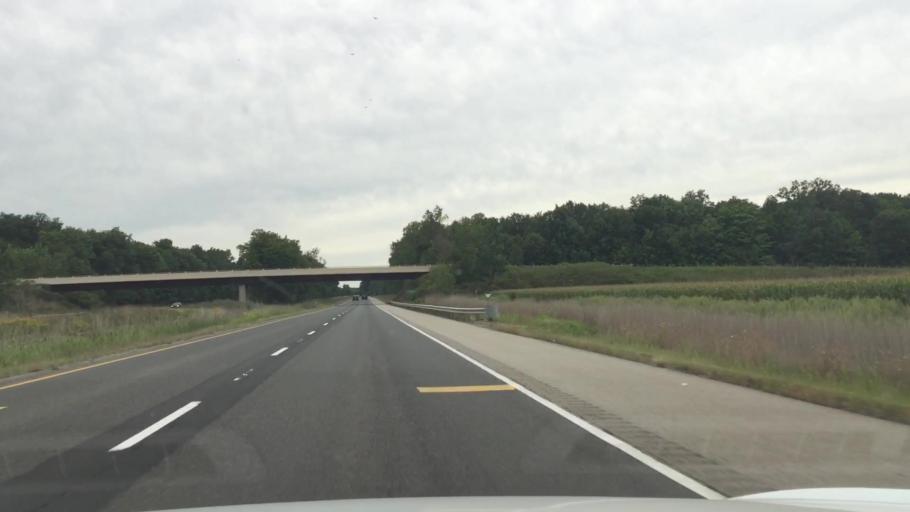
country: CA
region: Ontario
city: Lambton Shores
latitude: 42.9922
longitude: -81.9226
